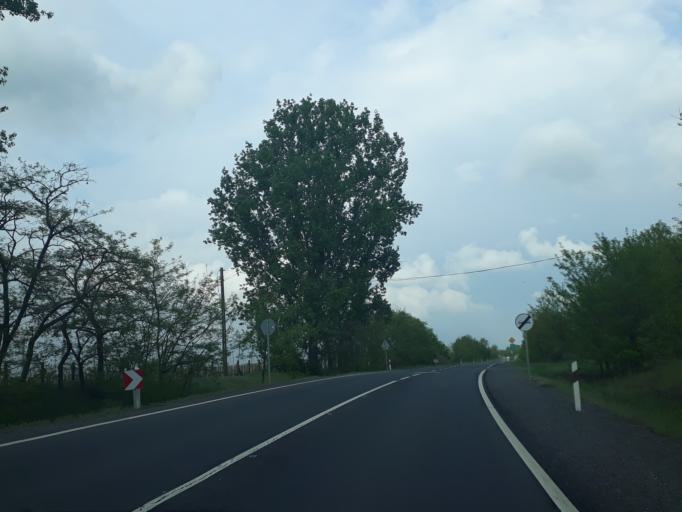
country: HU
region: Szabolcs-Szatmar-Bereg
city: Nyirtass
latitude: 48.1168
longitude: 21.9938
